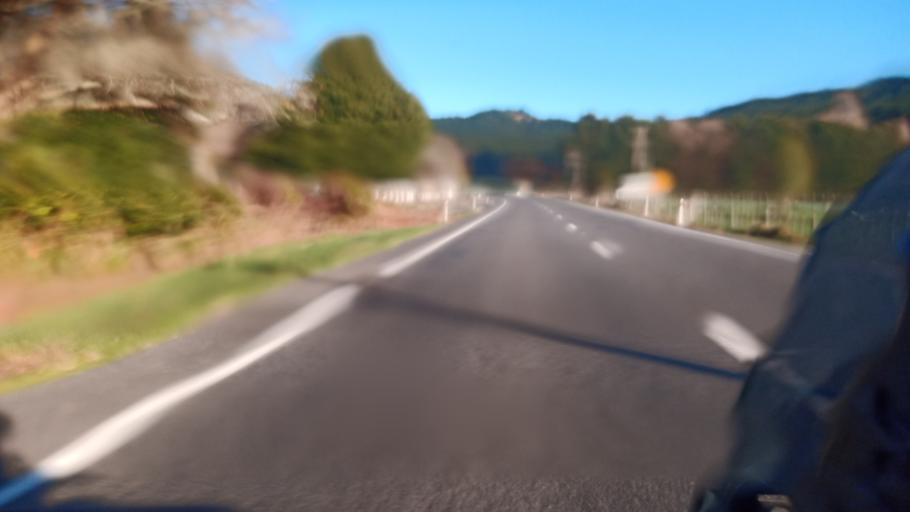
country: NZ
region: Hawke's Bay
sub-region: Wairoa District
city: Wairoa
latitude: -39.0206
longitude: 177.3227
